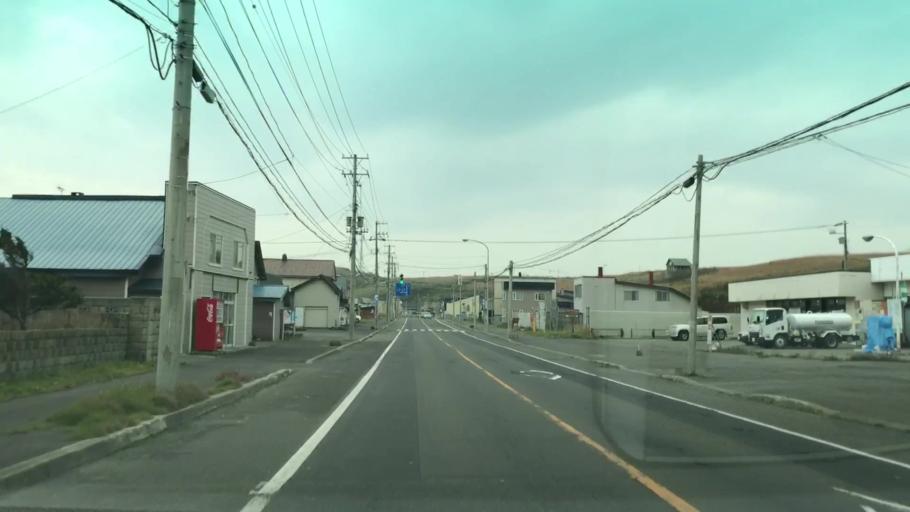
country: JP
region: Hokkaido
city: Ishikari
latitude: 43.3146
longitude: 141.4151
